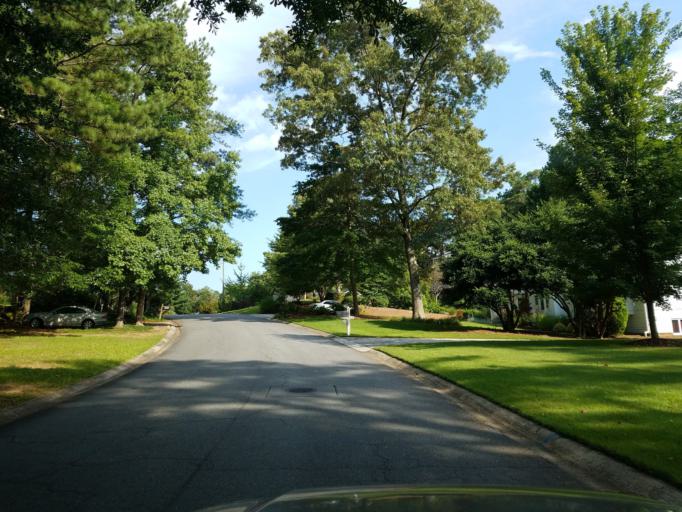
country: US
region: Georgia
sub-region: Fulton County
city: Sandy Springs
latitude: 33.9653
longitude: -84.4438
